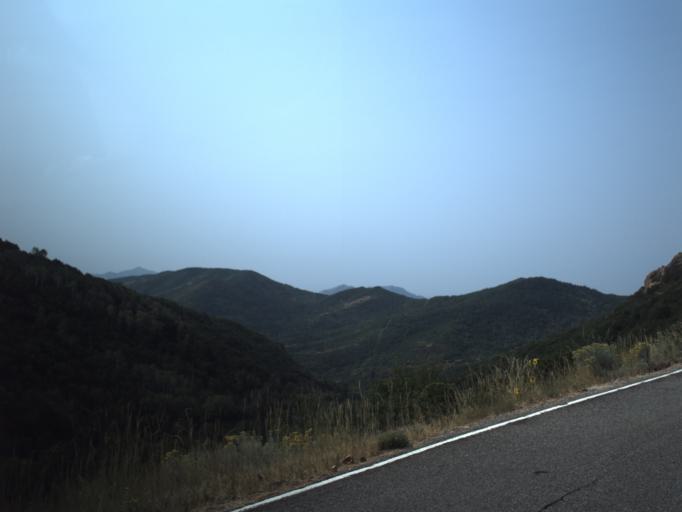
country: US
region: Utah
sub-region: Summit County
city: Summit Park
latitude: 40.8194
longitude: -111.6689
